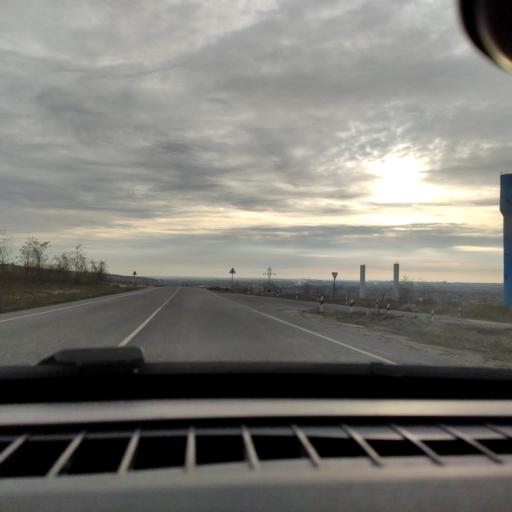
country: RU
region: Belgorod
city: Ilovka
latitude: 50.6468
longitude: 38.6317
